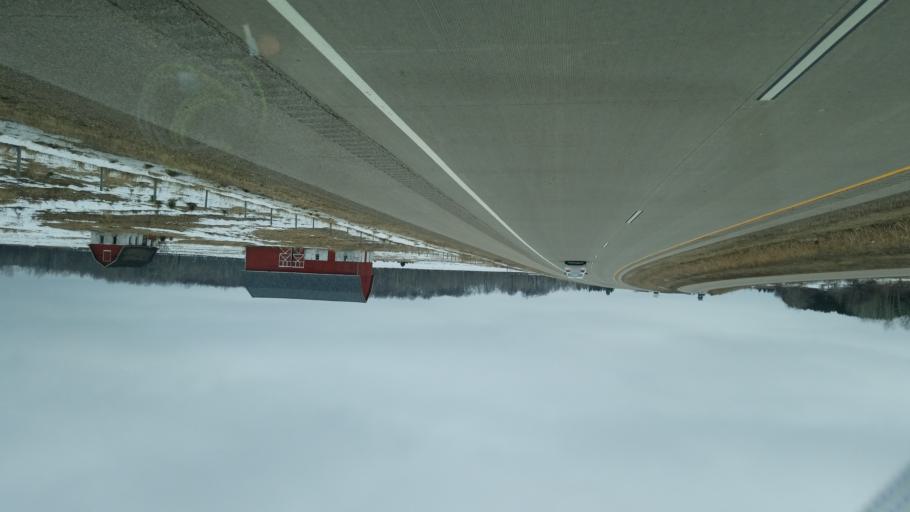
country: US
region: Wisconsin
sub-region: Portage County
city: Stevens Point
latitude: 44.5996
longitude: -89.7537
